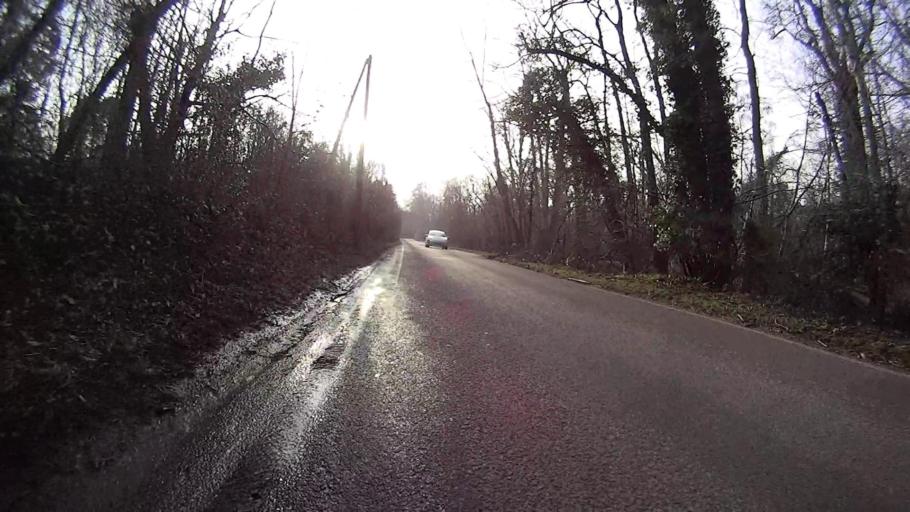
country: GB
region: England
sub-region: West Sussex
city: Copthorne
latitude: 51.1146
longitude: -0.1118
